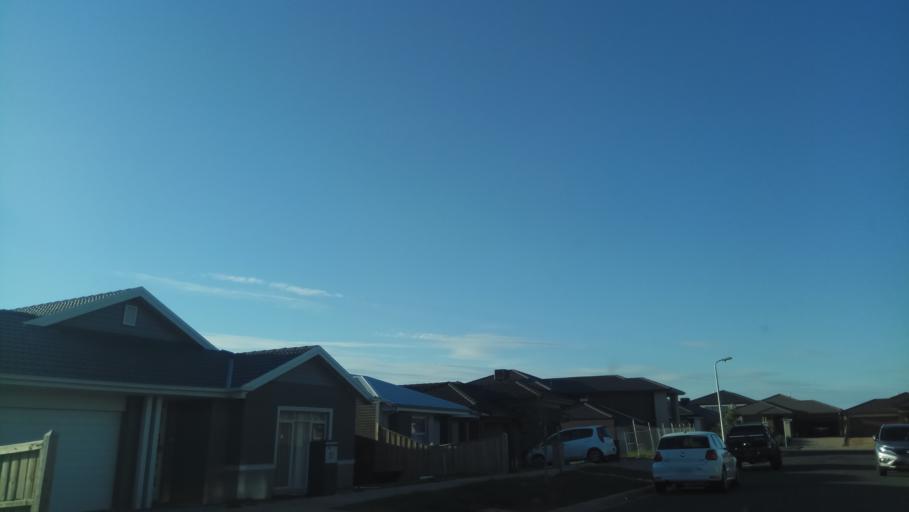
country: AU
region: Victoria
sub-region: Wyndham
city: Point Cook
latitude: -37.9103
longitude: 144.7446
